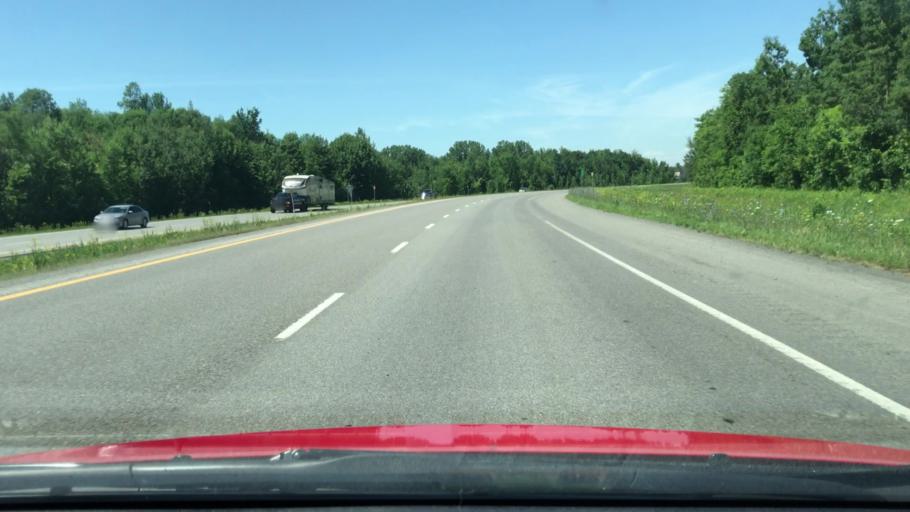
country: CA
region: Quebec
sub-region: Monteregie
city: Napierville
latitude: 45.2108
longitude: -73.4742
